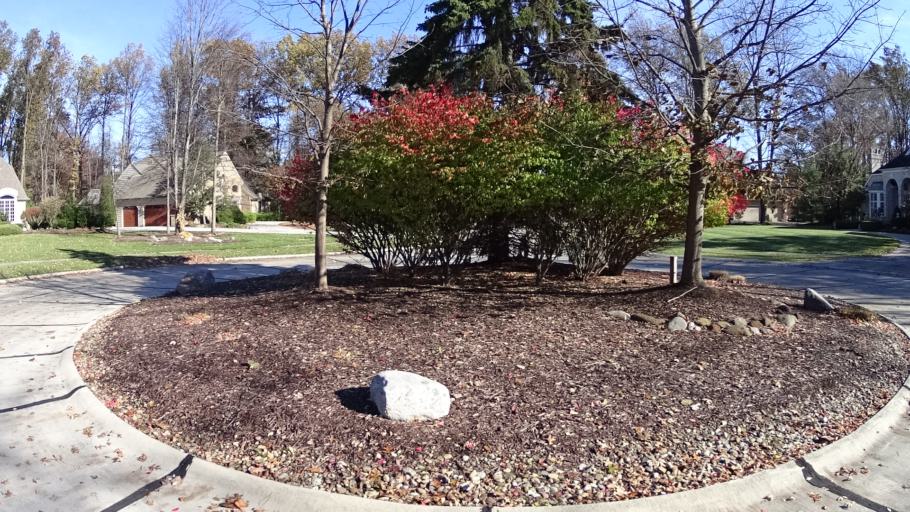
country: US
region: Ohio
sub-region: Lorain County
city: Avon Lake
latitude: 41.4941
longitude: -82.0018
